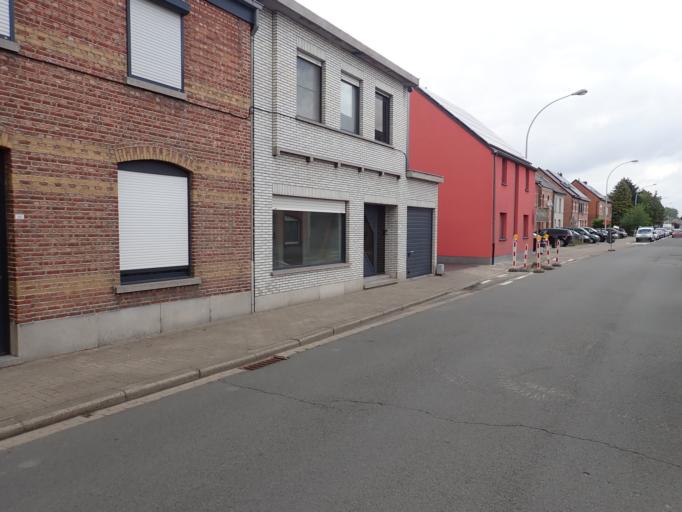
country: BE
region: Flanders
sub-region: Provincie Vlaams-Brabant
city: Londerzeel
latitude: 51.0301
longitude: 4.2970
